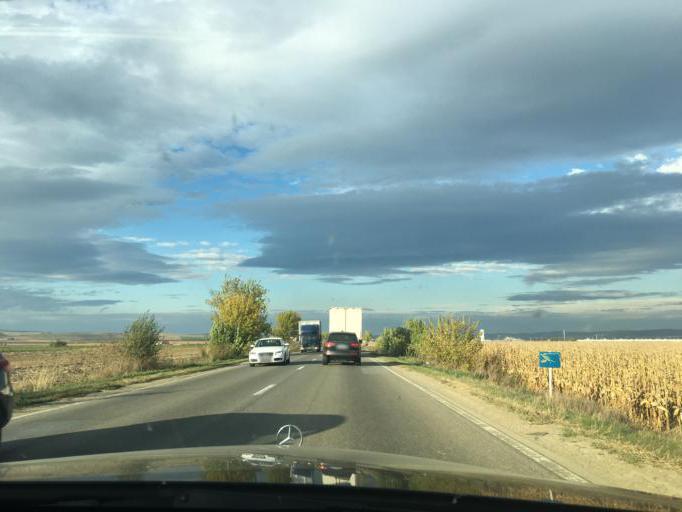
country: RO
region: Alba
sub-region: Comuna Galda de Jos
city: Galda de Jos
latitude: 46.1712
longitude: 23.6514
